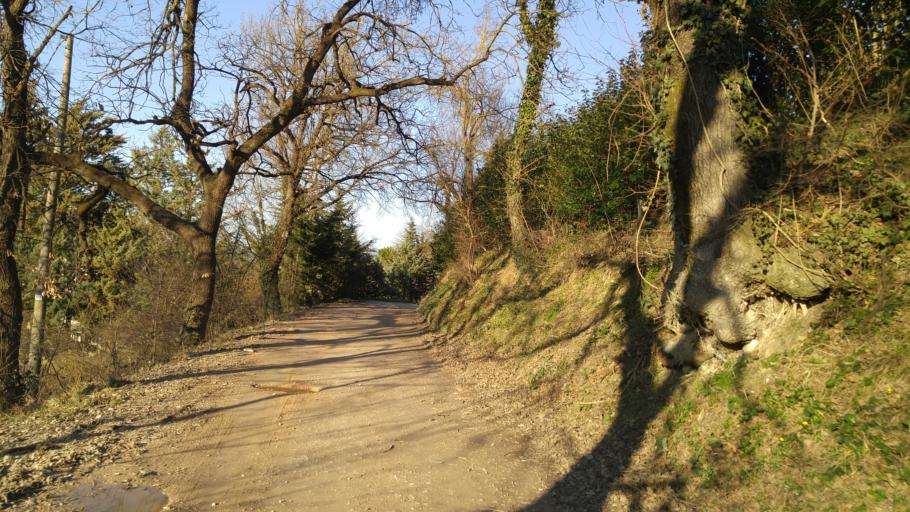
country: IT
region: The Marches
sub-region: Provincia di Pesaro e Urbino
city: Cagli
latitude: 43.5539
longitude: 12.6567
